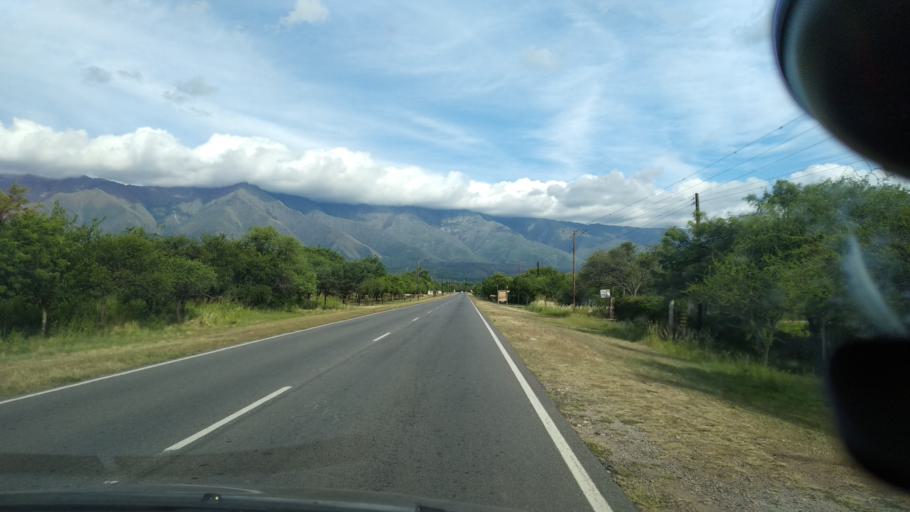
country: AR
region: Cordoba
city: Villa Las Rosas
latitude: -32.0069
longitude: -65.0592
